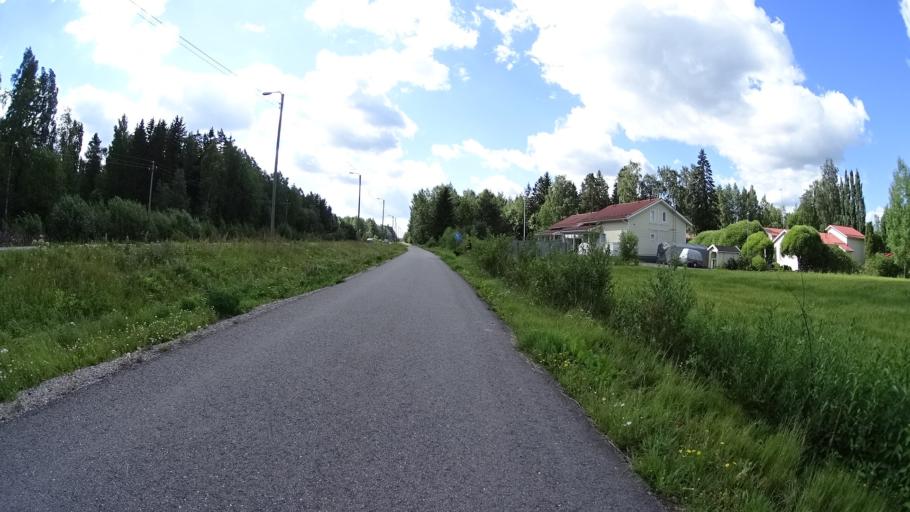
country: FI
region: Uusimaa
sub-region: Helsinki
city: Tuusula
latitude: 60.4280
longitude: 25.0539
